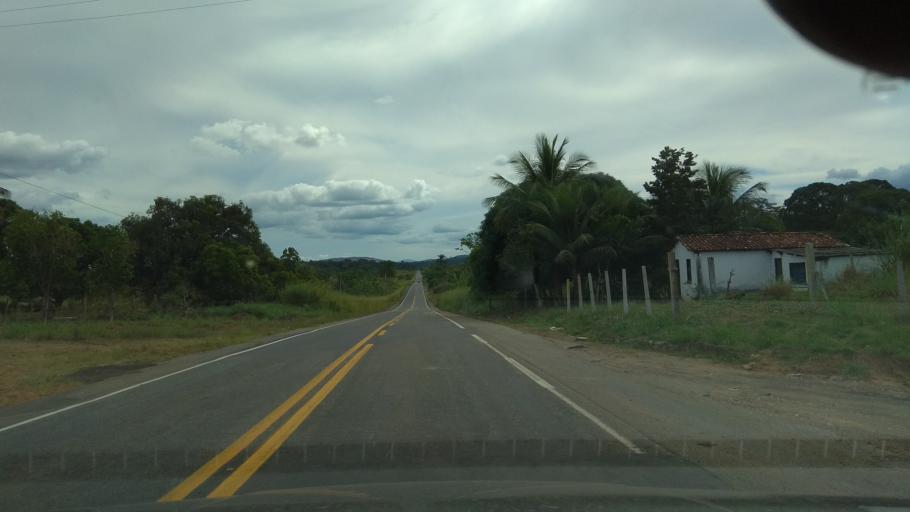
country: BR
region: Bahia
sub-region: Ubata
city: Ubata
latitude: -14.1962
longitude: -39.6263
